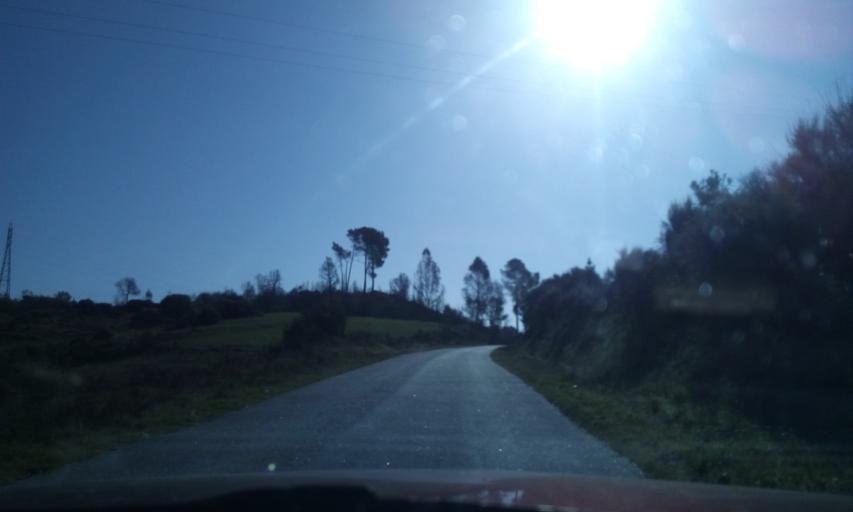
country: PT
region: Guarda
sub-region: Celorico da Beira
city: Celorico da Beira
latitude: 40.6896
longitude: -7.4194
